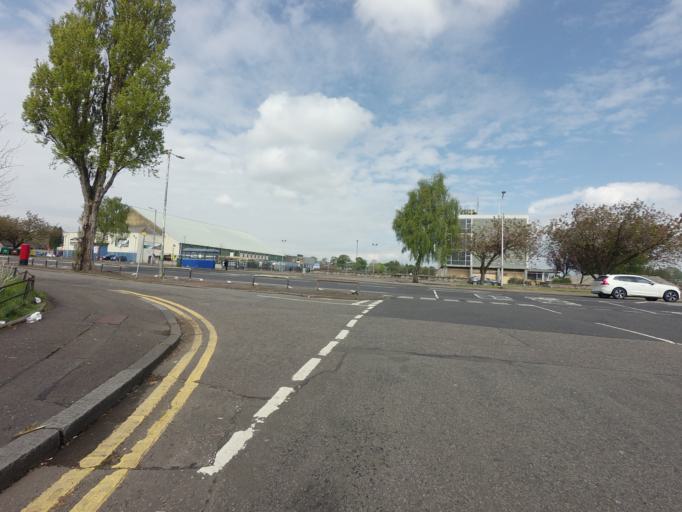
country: GB
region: Scotland
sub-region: Falkirk
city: Falkirk
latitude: 56.0038
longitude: -3.7673
